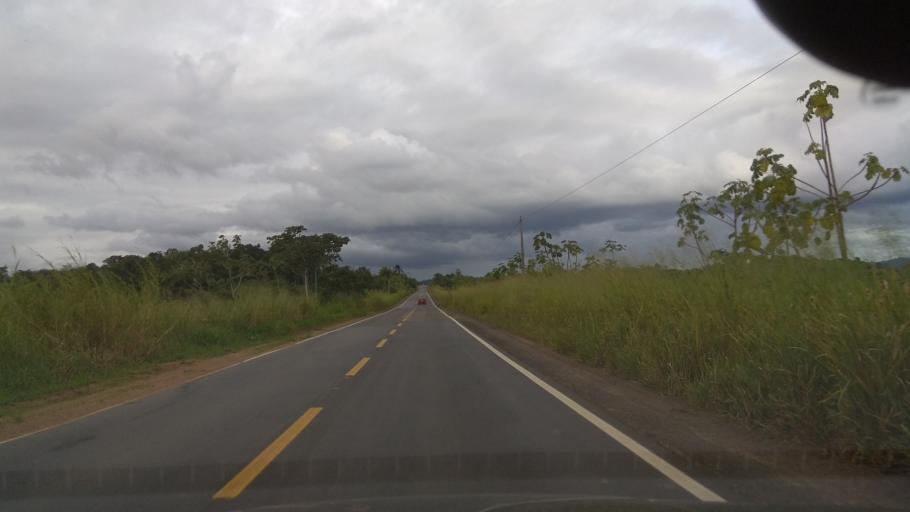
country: BR
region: Bahia
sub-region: Ubata
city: Ubata
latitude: -14.1952
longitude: -39.6352
